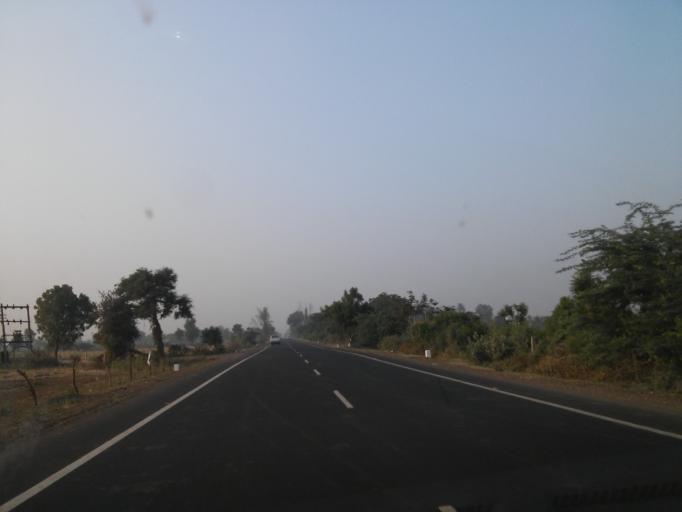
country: IN
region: Gujarat
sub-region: Kachchh
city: Mandvi
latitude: 22.8722
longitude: 69.3945
